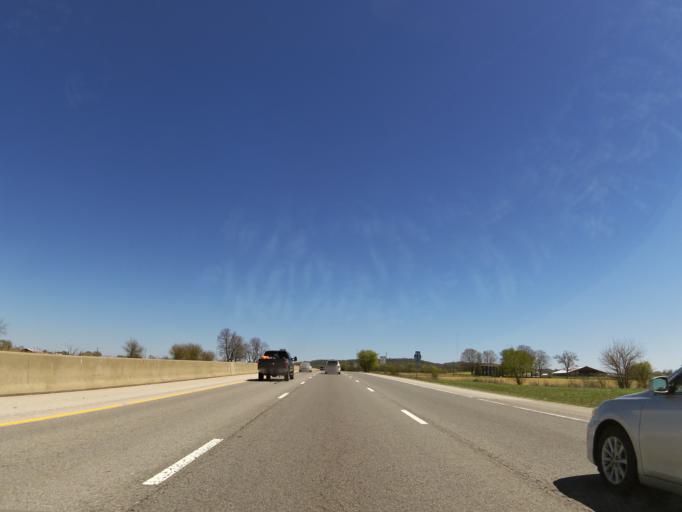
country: US
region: Kentucky
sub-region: Edmonson County
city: Brownsville
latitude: 37.0417
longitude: -86.2036
